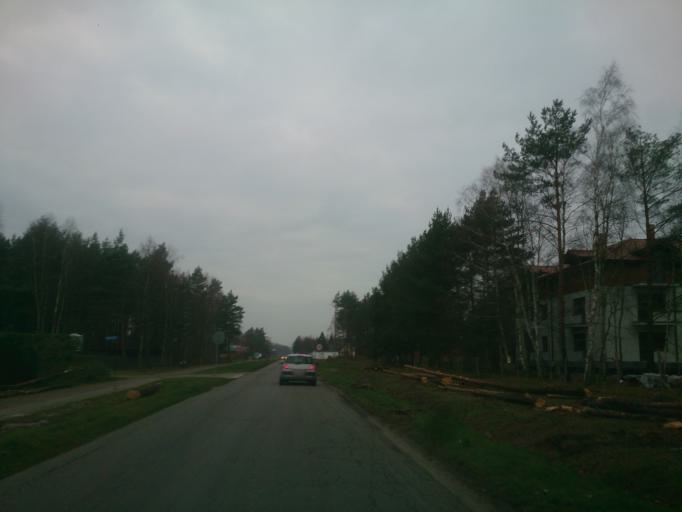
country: PL
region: West Pomeranian Voivodeship
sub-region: Powiat slawienski
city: Darlowo
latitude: 54.3907
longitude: 16.3371
